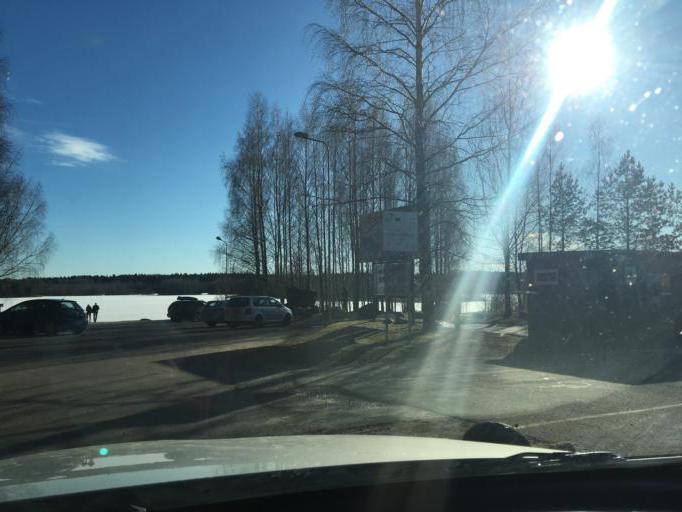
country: LV
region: Jekabpils Rajons
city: Jekabpils
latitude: 56.4825
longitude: 25.8520
